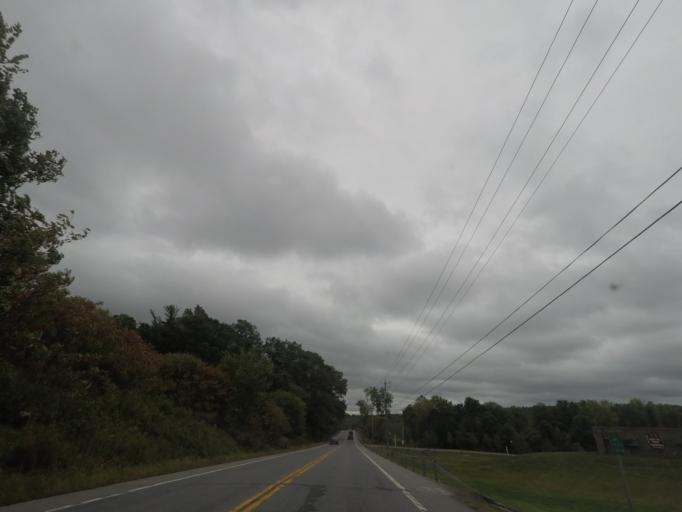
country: US
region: New York
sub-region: Saratoga County
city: Country Knolls
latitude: 42.9267
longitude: -73.7600
